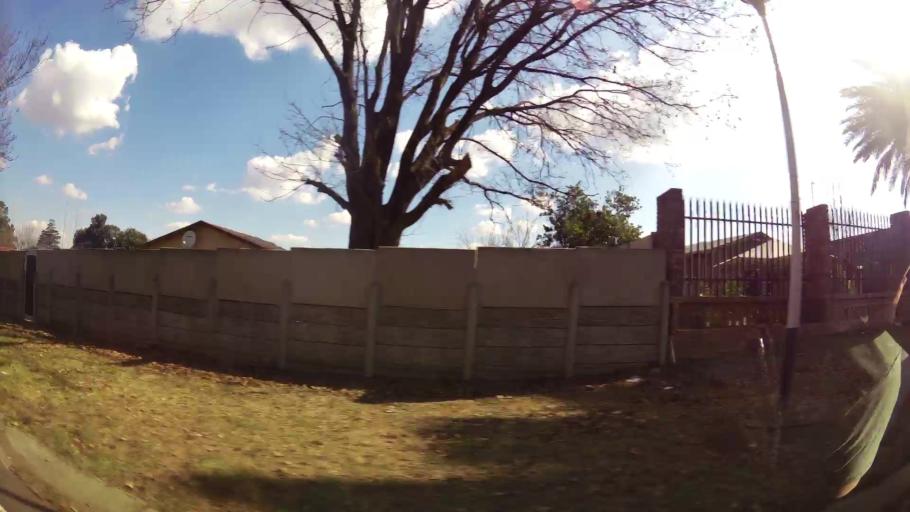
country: ZA
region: Mpumalanga
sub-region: Nkangala District Municipality
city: Witbank
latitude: -25.9150
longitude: 29.2308
